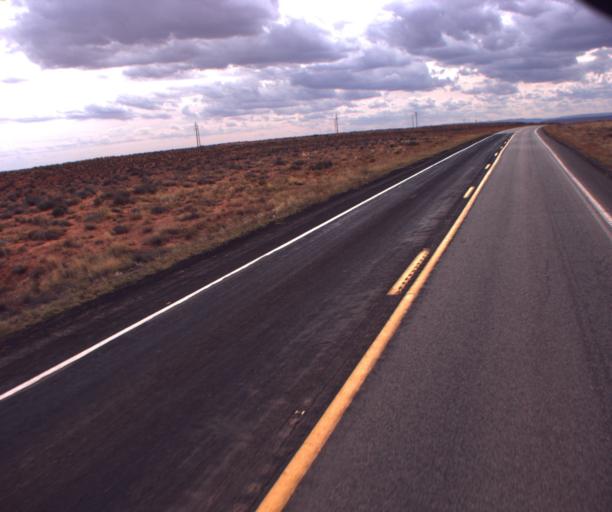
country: US
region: Arizona
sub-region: Navajo County
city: Kayenta
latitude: 36.9009
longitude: -109.7908
